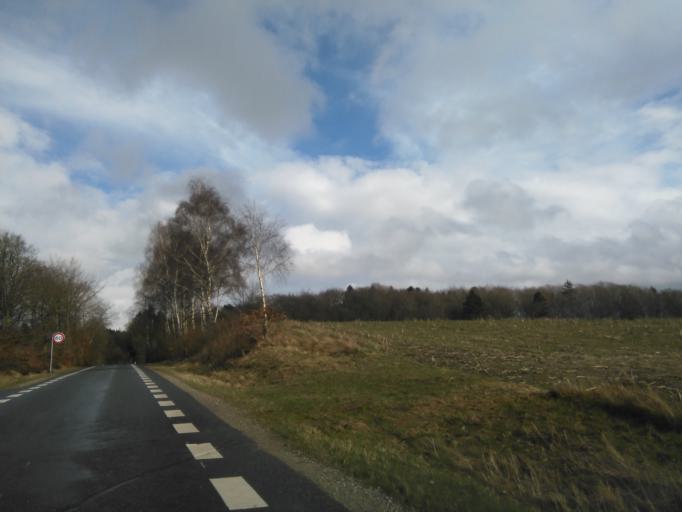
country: DK
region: Central Jutland
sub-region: Skanderborg Kommune
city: Ry
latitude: 56.1082
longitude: 9.7911
